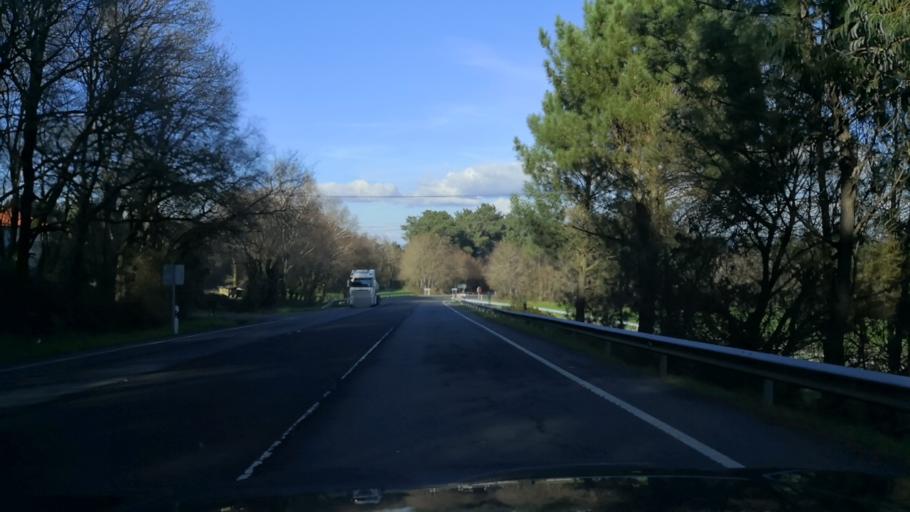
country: ES
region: Galicia
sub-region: Provincia de Pontevedra
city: Silleda
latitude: 42.7028
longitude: -8.3110
